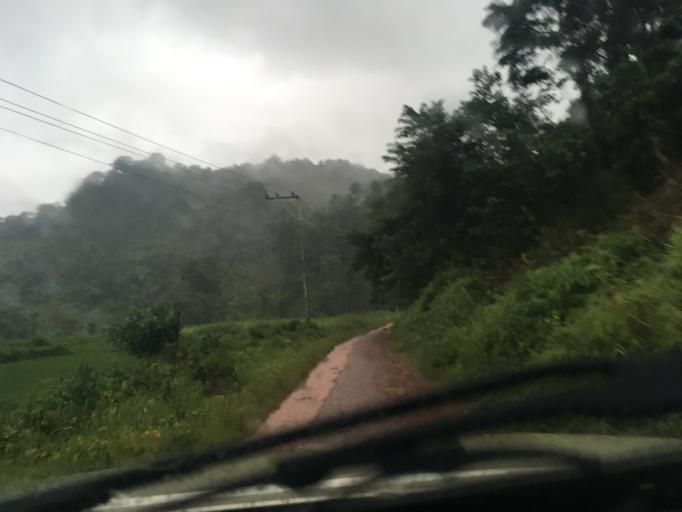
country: LA
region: Oudomxai
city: Muang La
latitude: 21.2269
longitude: 101.9624
